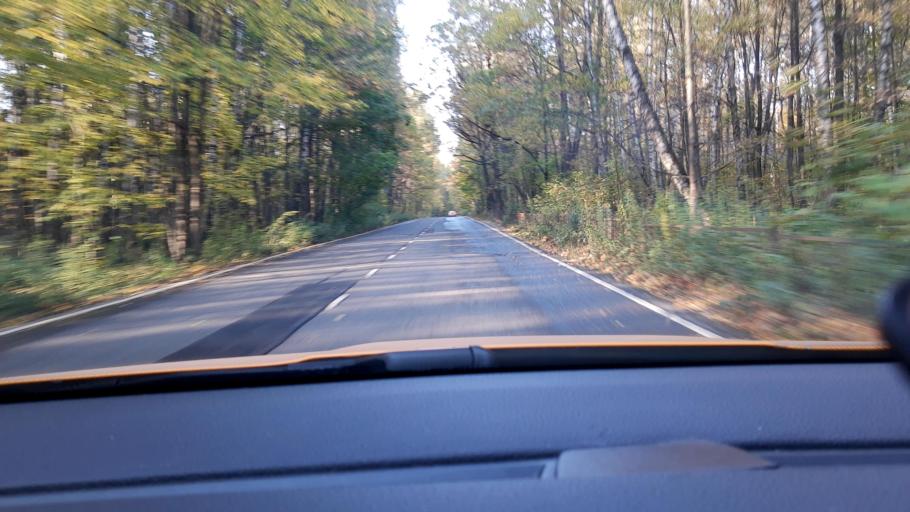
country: RU
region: Moskovskaya
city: Bogorodskoye
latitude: 55.8303
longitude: 37.7458
